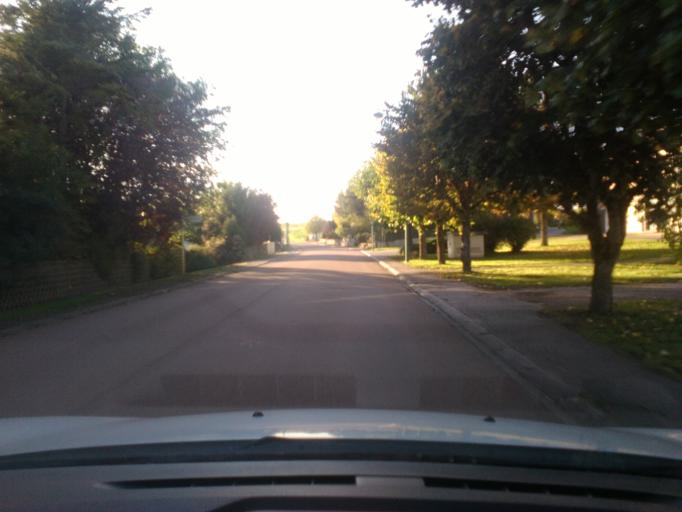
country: FR
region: Lorraine
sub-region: Departement des Vosges
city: Chatel-sur-Moselle
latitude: 48.3228
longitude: 6.4590
